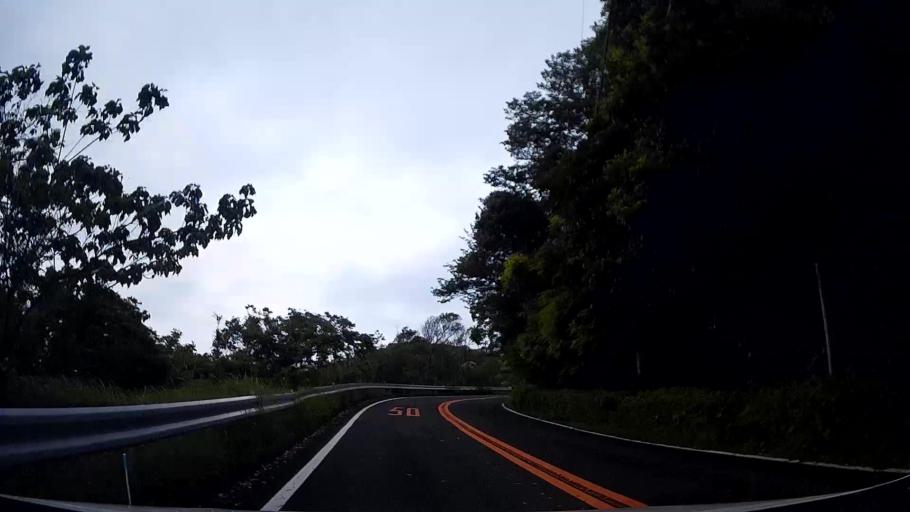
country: JP
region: Shizuoka
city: Shimoda
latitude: 34.6745
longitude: 138.7825
